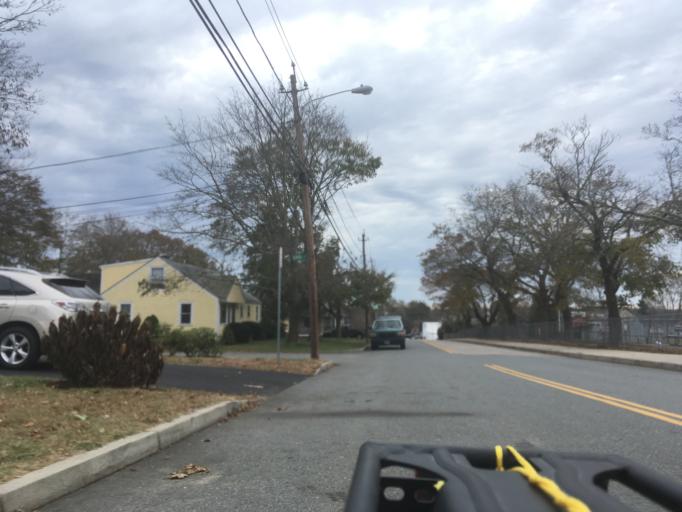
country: US
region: Rhode Island
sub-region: Kent County
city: East Greenwich
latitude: 41.6578
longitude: -71.4554
